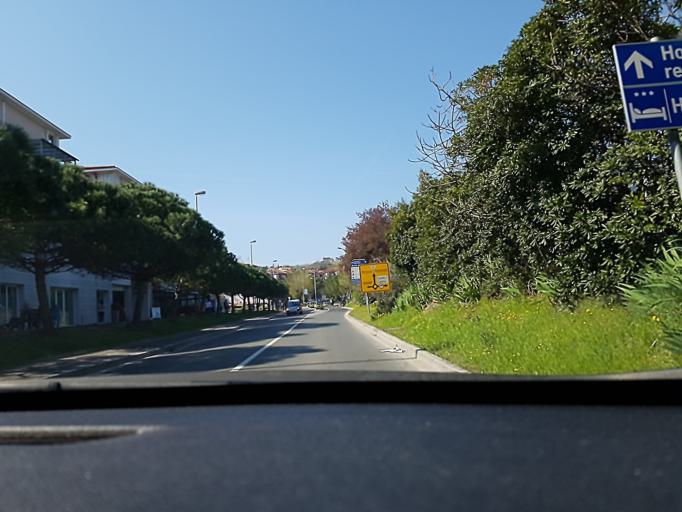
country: SI
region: Izola-Isola
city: Jagodje
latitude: 45.5306
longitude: 13.6524
